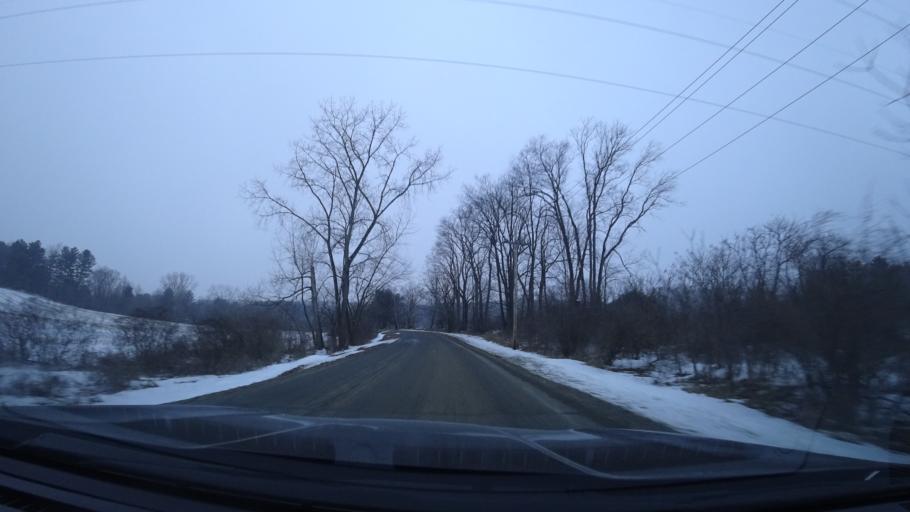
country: US
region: New York
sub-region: Washington County
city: Cambridge
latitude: 43.1608
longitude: -73.3645
